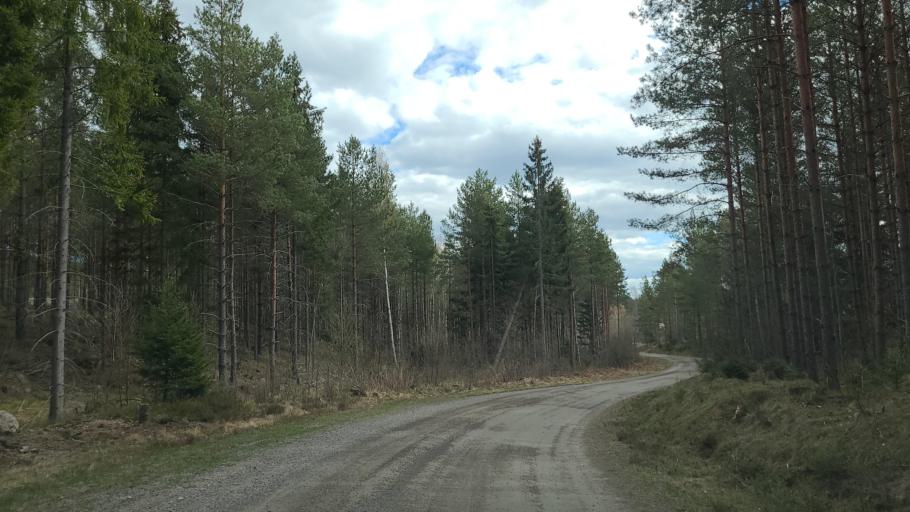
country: SE
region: OEstergoetland
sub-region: Norrkopings Kommun
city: Krokek
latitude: 58.6825
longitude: 16.4244
